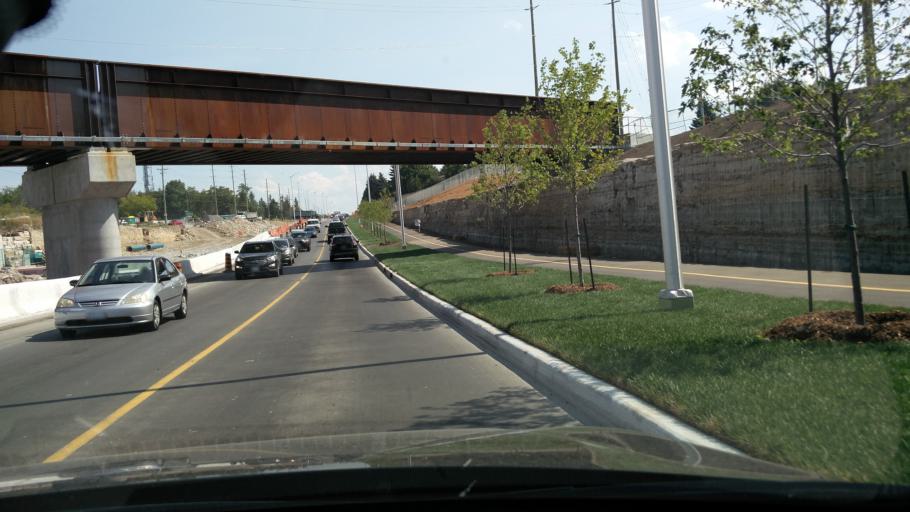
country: CA
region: Ontario
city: Bells Corners
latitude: 45.2798
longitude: -75.7521
